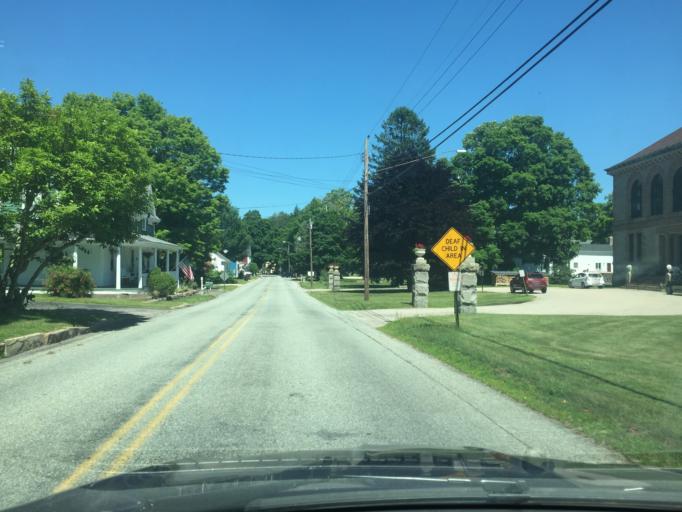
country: US
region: Connecticut
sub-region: New London County
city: Pawcatuck
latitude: 41.4402
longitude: -71.8855
